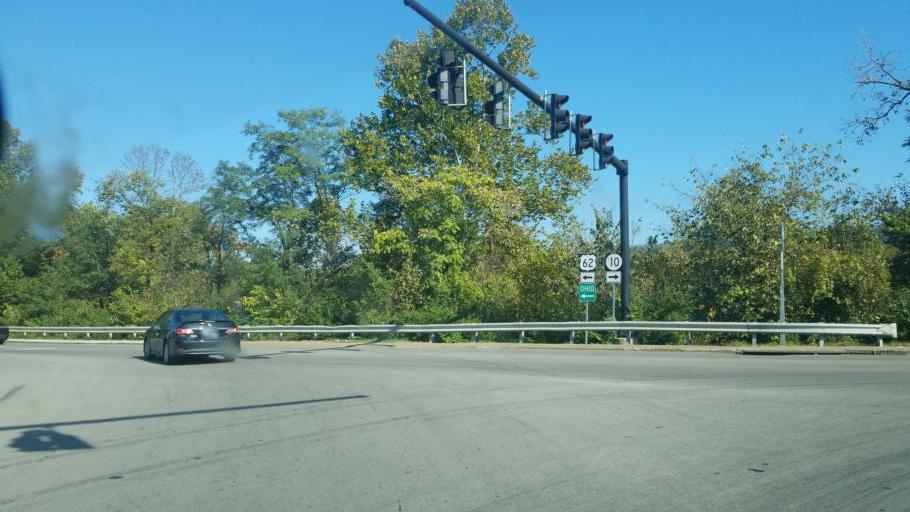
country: US
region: Ohio
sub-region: Brown County
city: Aberdeen
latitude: 38.6437
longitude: -83.7584
